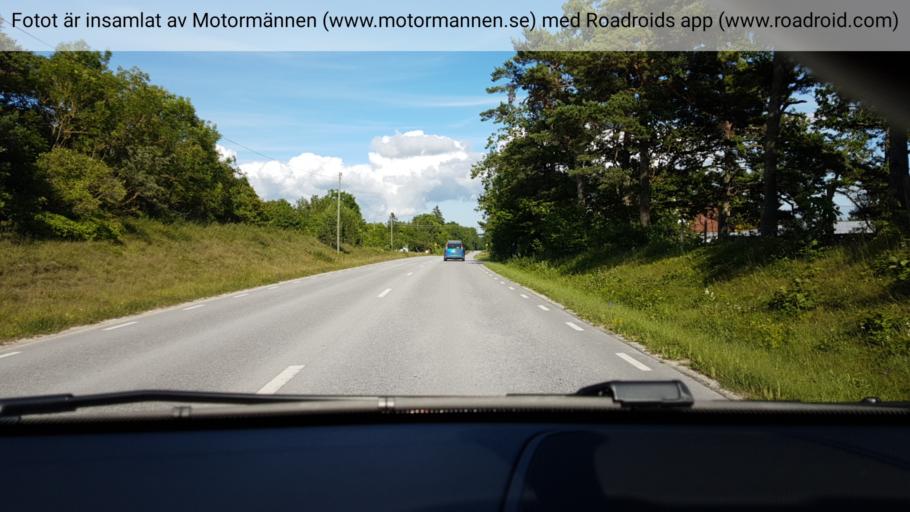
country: SE
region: Gotland
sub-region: Gotland
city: Slite
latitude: 57.7487
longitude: 18.7076
